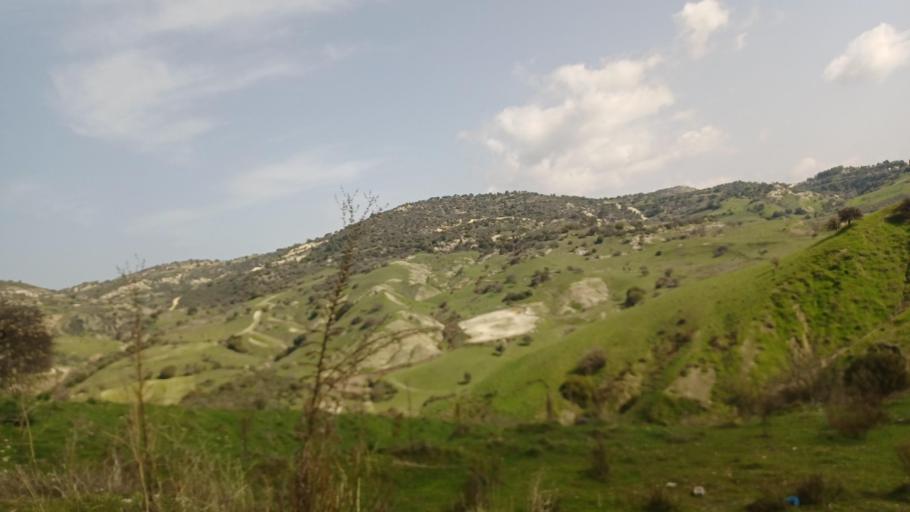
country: CY
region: Limassol
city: Pissouri
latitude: 34.7498
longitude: 32.6596
